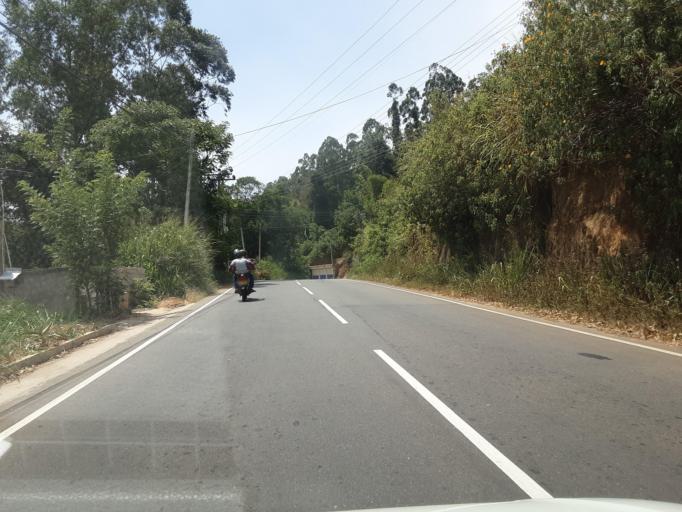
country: LK
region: Central
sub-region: Nuwara Eliya District
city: Nuwara Eliya
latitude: 6.9346
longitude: 80.9071
